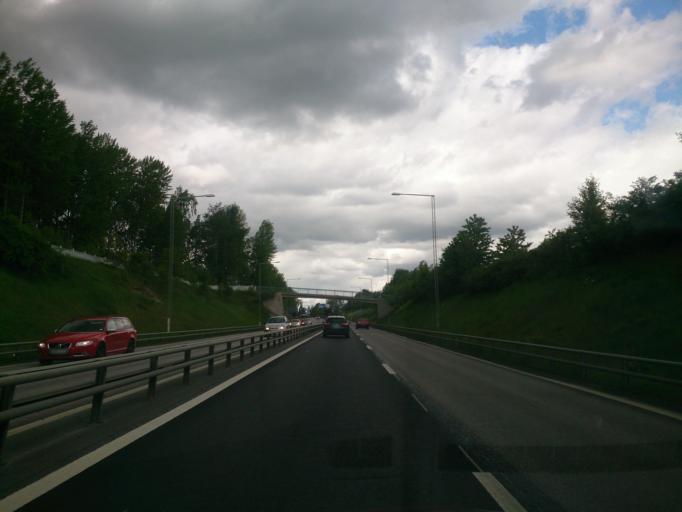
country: SE
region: OEstergoetland
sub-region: Norrkopings Kommun
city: Norrkoping
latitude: 58.5810
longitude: 16.1543
